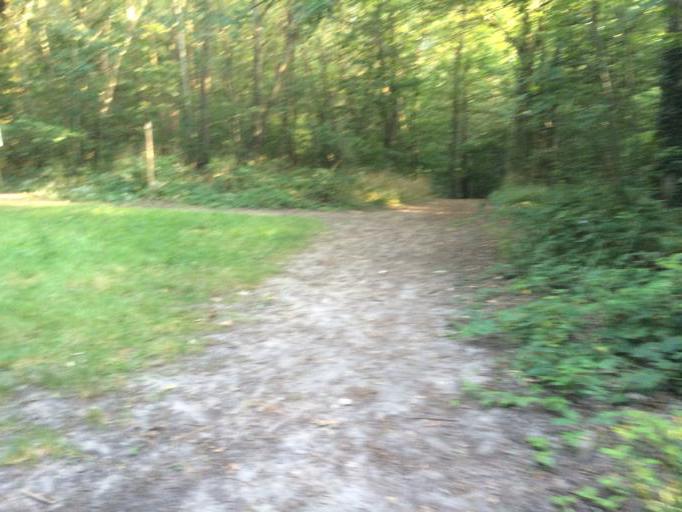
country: FR
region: Ile-de-France
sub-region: Departement de l'Essonne
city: Les Ulis
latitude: 48.6901
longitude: 2.1583
